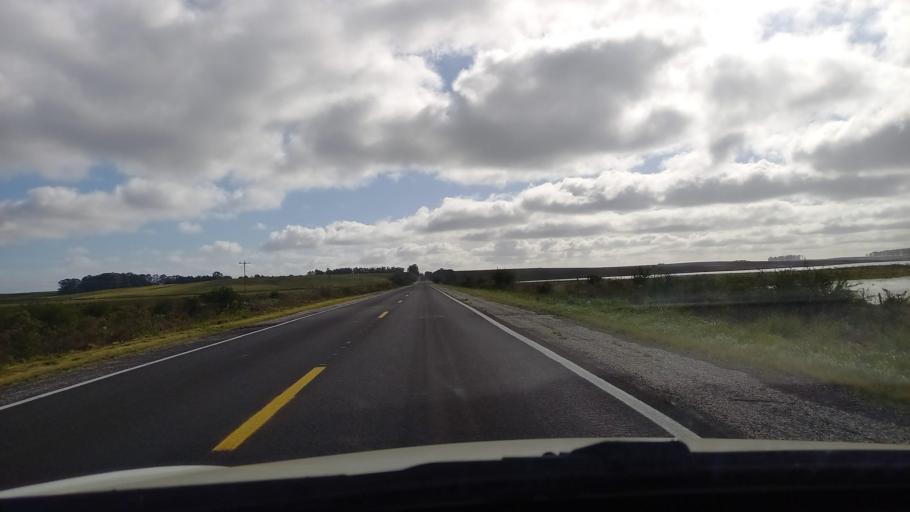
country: BR
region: Rio Grande do Sul
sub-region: Dom Pedrito
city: Dom Pedrito
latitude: -30.8862
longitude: -54.8724
